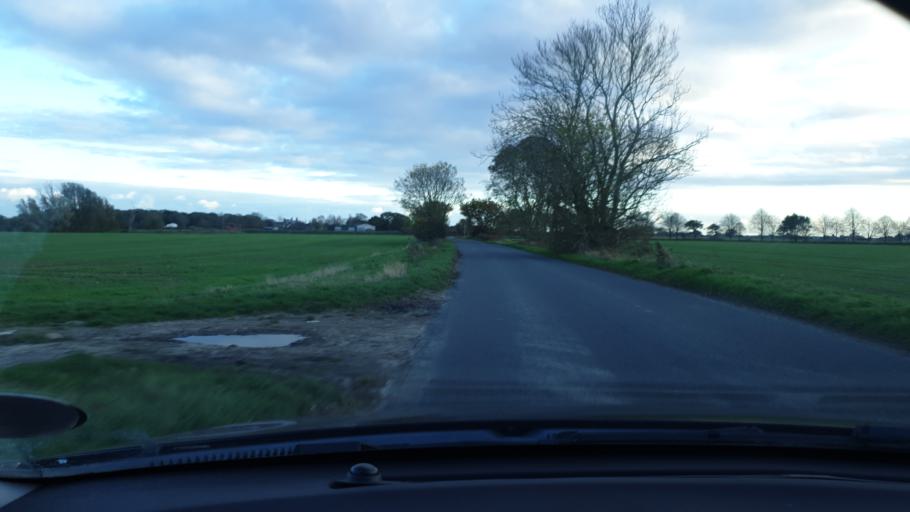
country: GB
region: England
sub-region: Essex
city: Little Clacton
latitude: 51.8929
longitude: 1.1478
